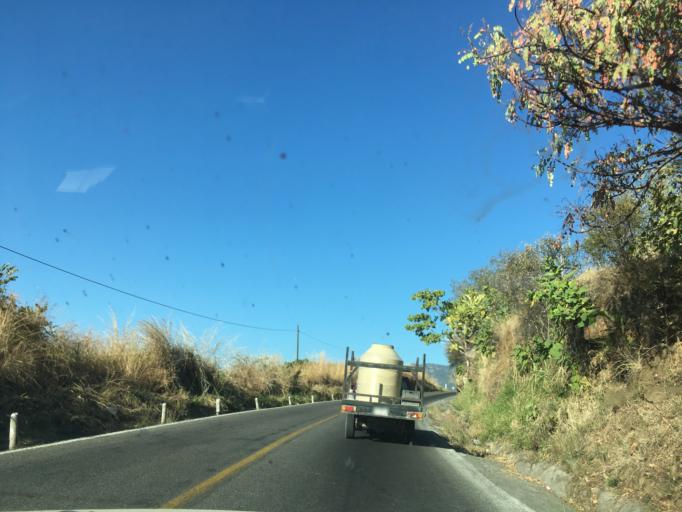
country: MX
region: Michoacan
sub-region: Gabriel Zamora
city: Lombardia
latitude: 19.1885
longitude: -102.0620
